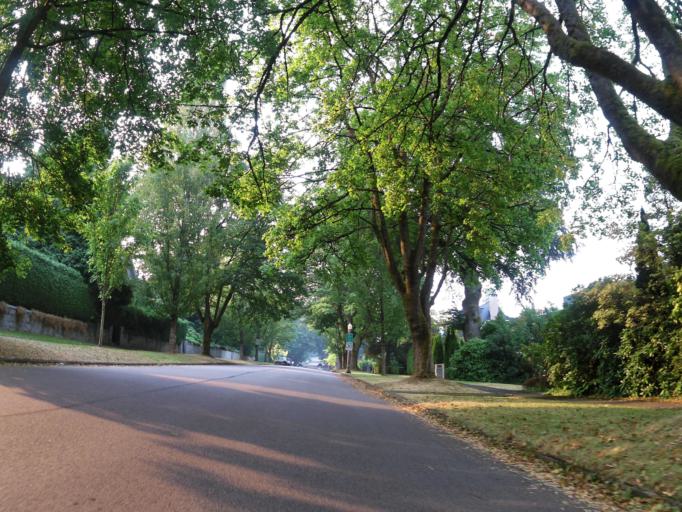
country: CA
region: British Columbia
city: Vancouver
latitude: 49.2432
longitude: -123.1456
